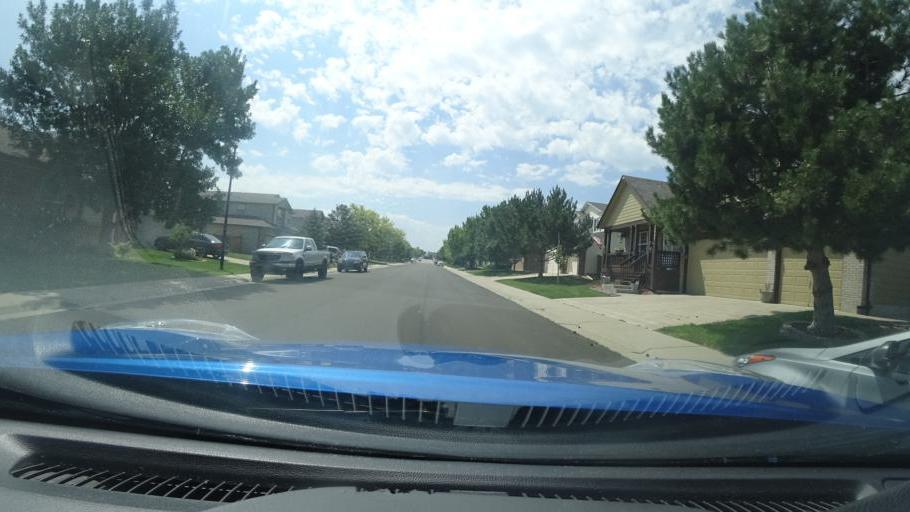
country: US
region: Colorado
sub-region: Adams County
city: Aurora
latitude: 39.6765
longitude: -104.7542
